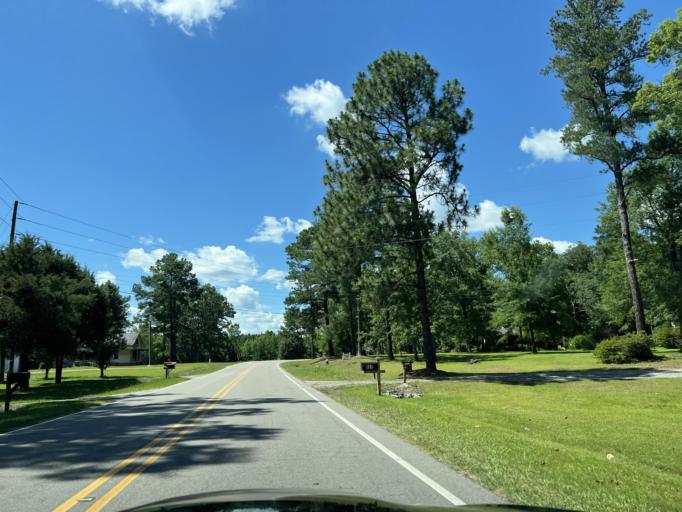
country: US
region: North Carolina
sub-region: Lee County
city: Sanford
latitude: 35.4394
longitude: -79.1724
